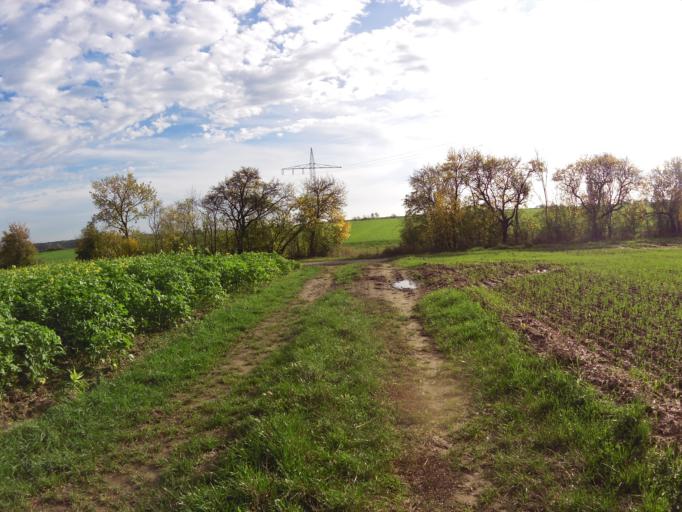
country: DE
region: Bavaria
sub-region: Regierungsbezirk Unterfranken
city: Biebelried
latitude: 49.7289
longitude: 10.0708
